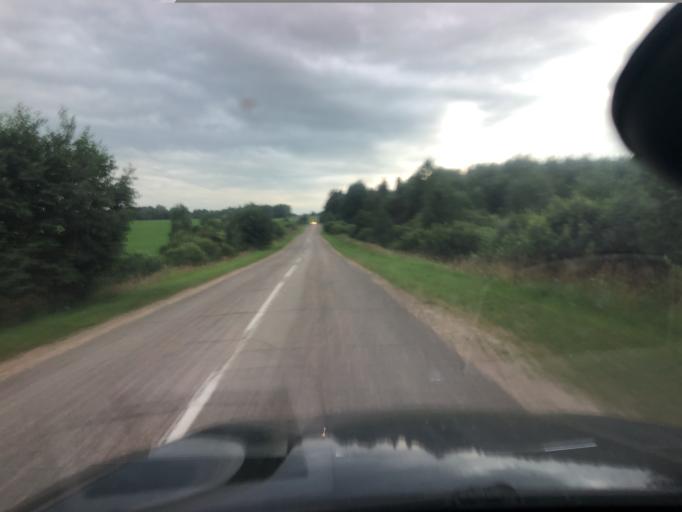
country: RU
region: Jaroslavl
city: Pereslavl'-Zalesskiy
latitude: 57.0203
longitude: 38.9488
